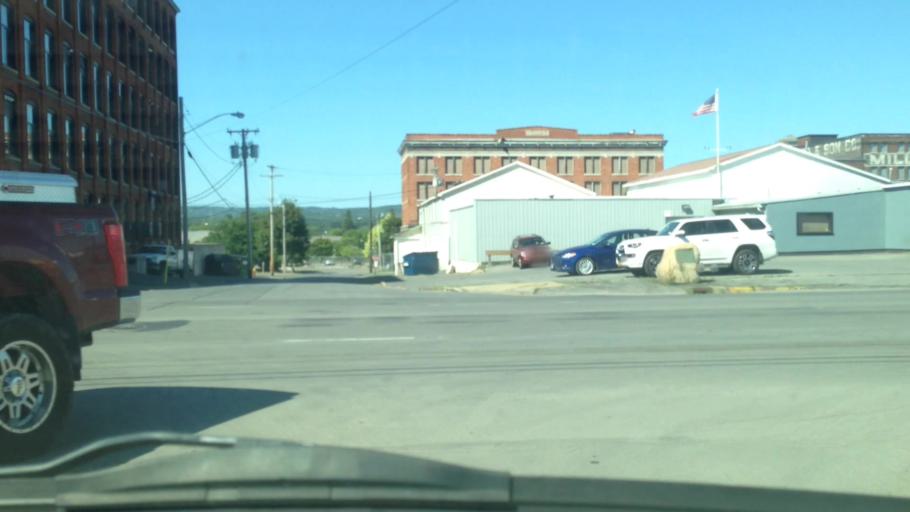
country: US
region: New York
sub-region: Oneida County
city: Utica
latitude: 43.1021
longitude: -75.2216
